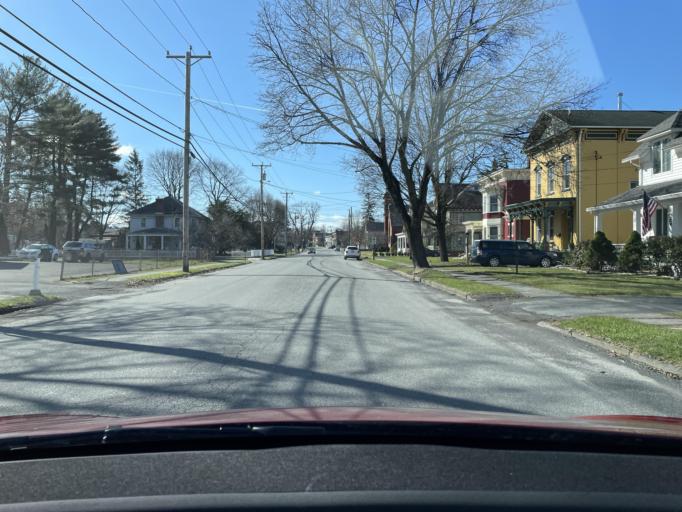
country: US
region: New York
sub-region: Ulster County
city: Saugerties
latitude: 42.0804
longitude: -73.9548
